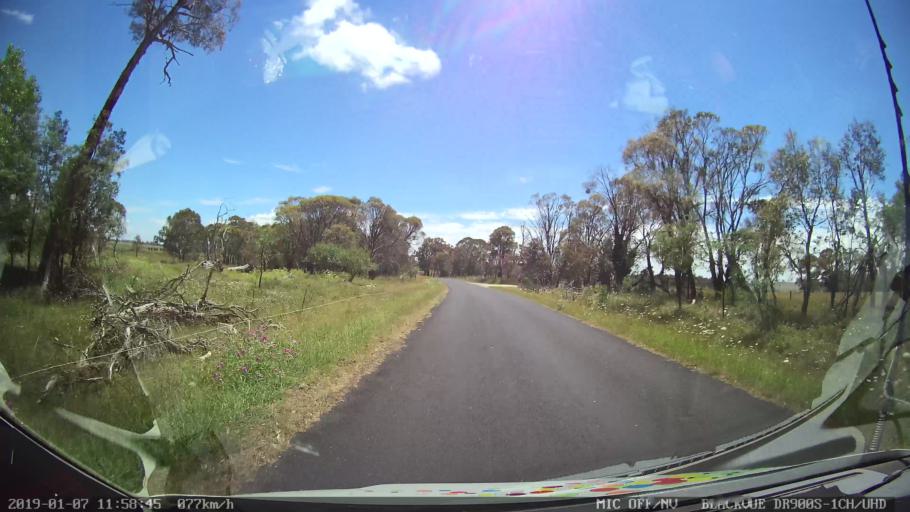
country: AU
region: New South Wales
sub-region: Guyra
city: Guyra
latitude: -30.2498
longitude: 151.6682
